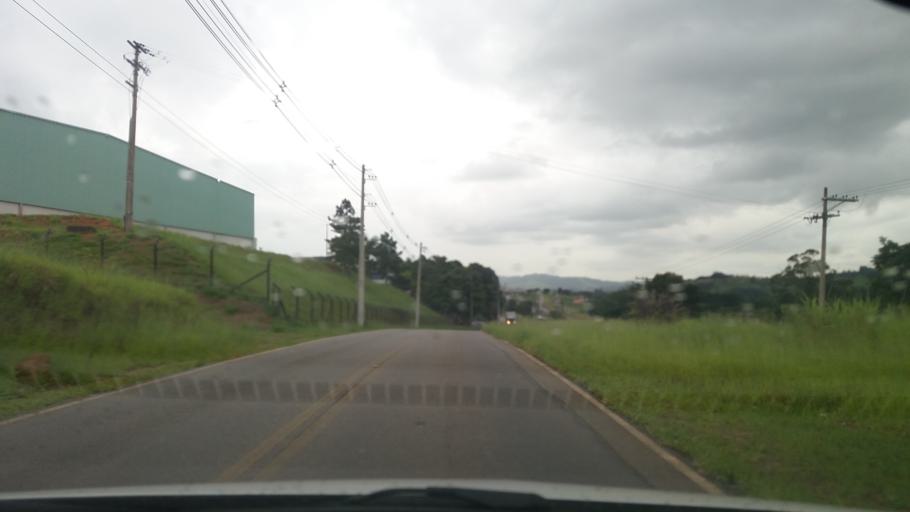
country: BR
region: Sao Paulo
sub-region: Bom Jesus Dos Perdoes
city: Bom Jesus dos Perdoes
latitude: -23.1682
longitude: -46.4442
